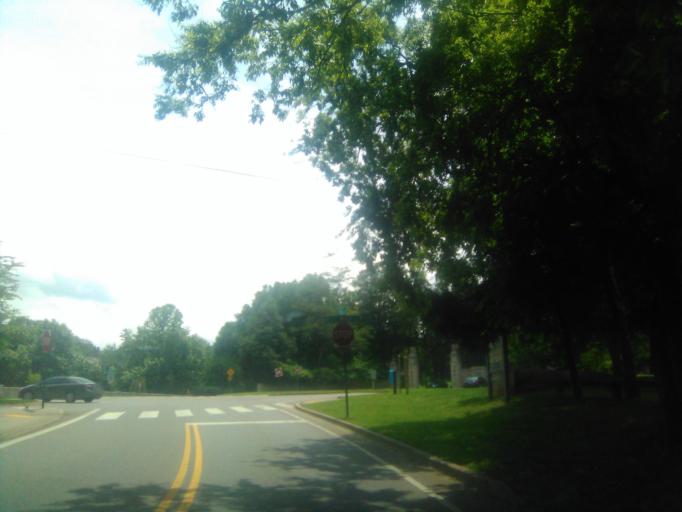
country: US
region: Tennessee
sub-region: Davidson County
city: Belle Meade
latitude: 36.0835
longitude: -86.8670
